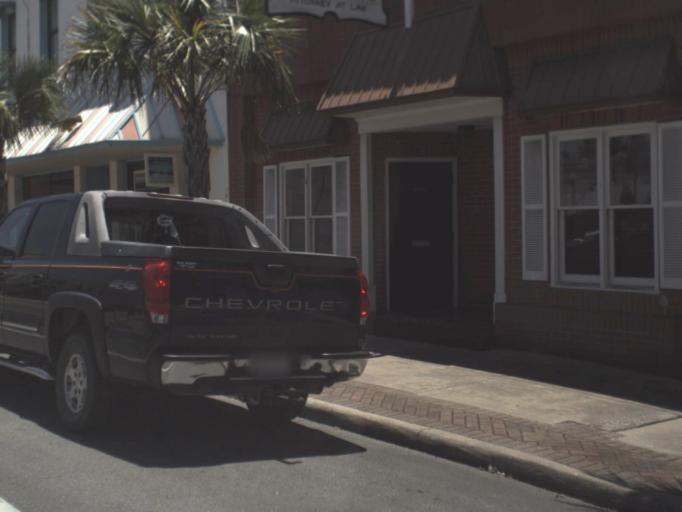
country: US
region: Florida
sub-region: Suwannee County
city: Live Oak
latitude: 30.2959
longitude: -82.9838
